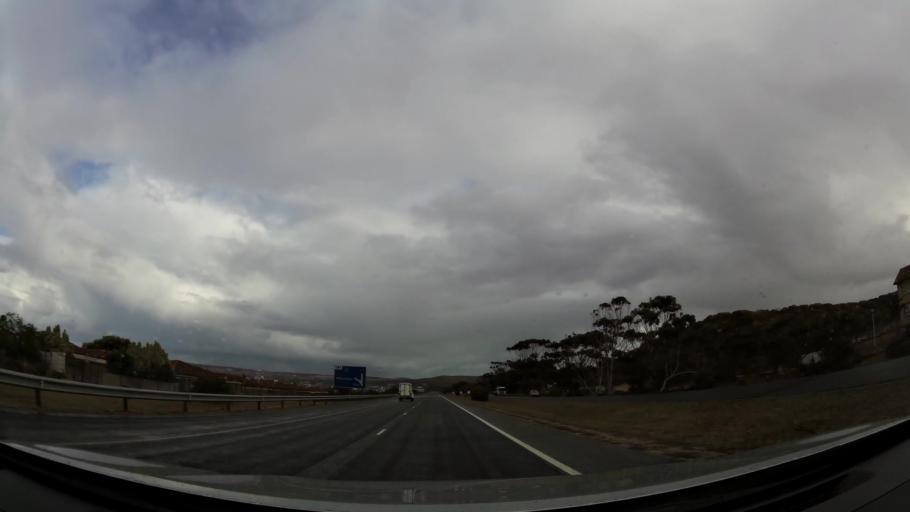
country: ZA
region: Western Cape
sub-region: Eden District Municipality
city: Mossel Bay
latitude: -34.1317
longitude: 22.1024
